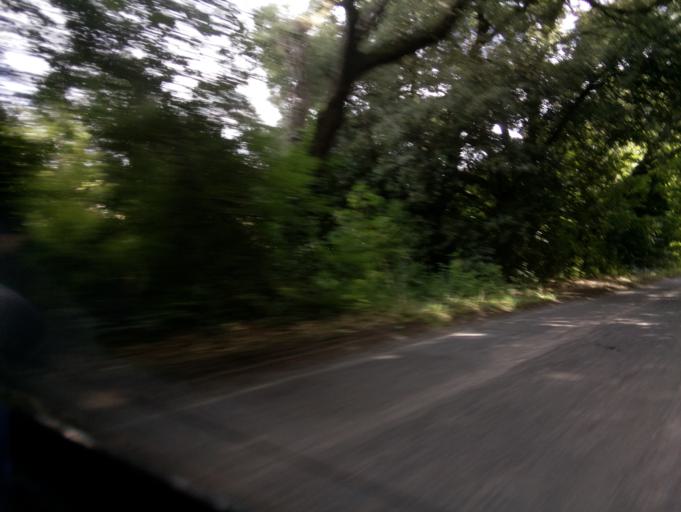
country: GB
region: England
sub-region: Gloucestershire
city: Stonehouse
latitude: 51.7886
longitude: -2.2734
